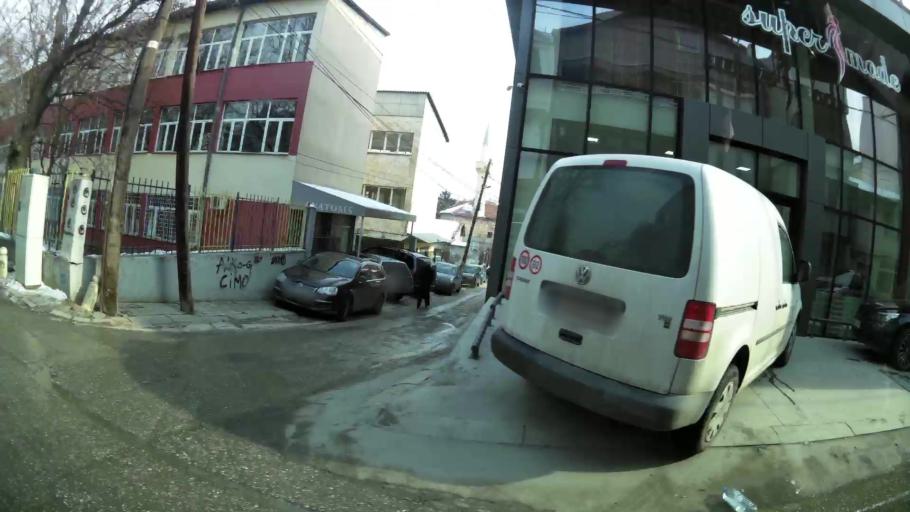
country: MK
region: Karpos
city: Skopje
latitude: 42.0047
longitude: 21.4360
